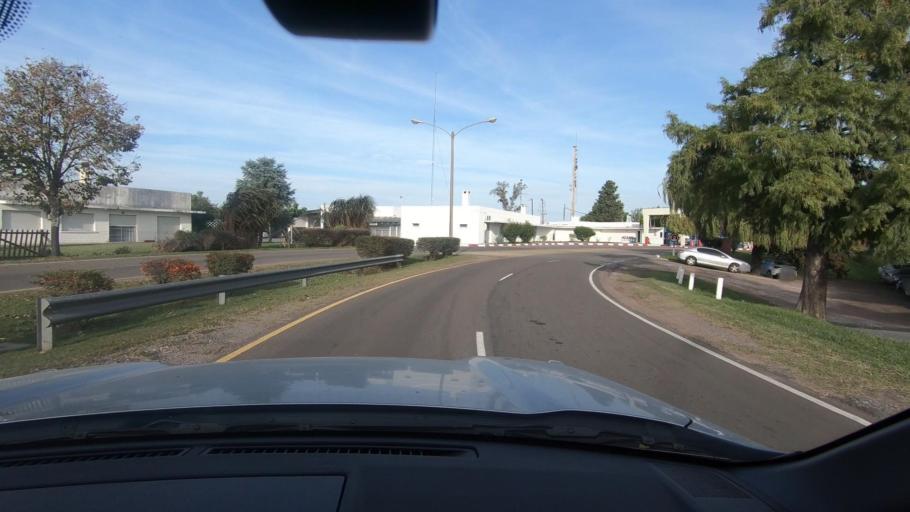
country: AR
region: Entre Rios
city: Colon
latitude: -32.2471
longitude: -58.1444
